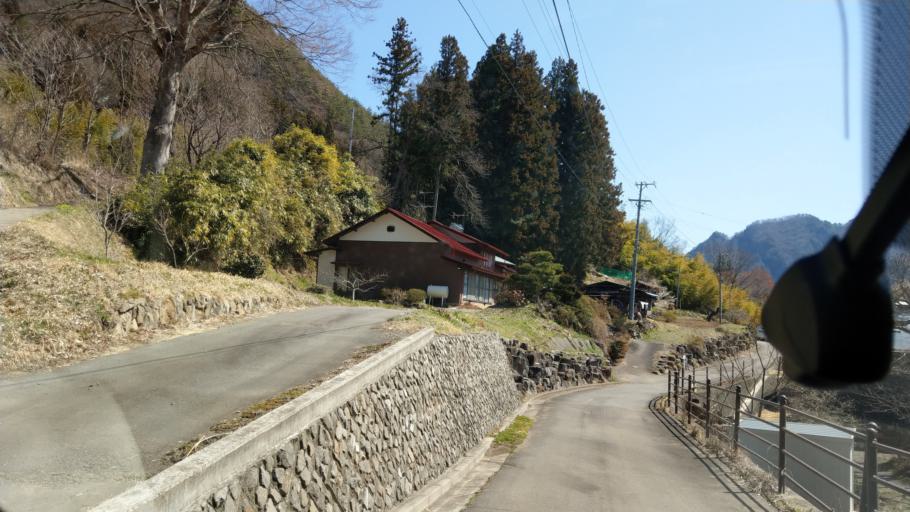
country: JP
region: Nagano
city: Kamimaruko
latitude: 36.3361
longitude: 138.1587
